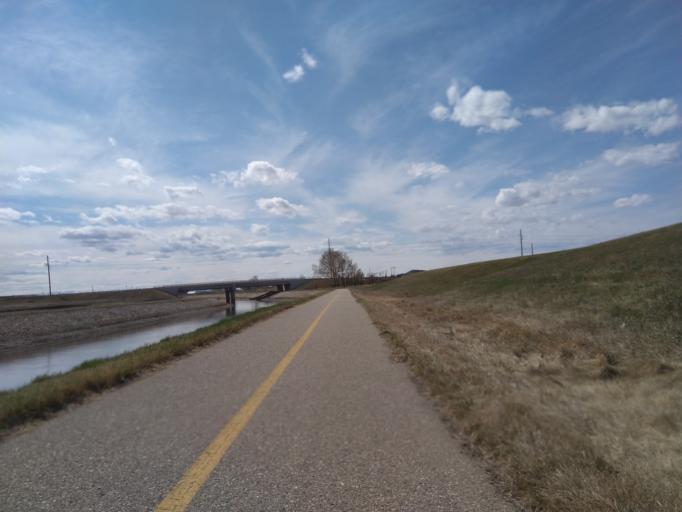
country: CA
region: Alberta
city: Chestermere
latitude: 50.9721
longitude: -113.9315
